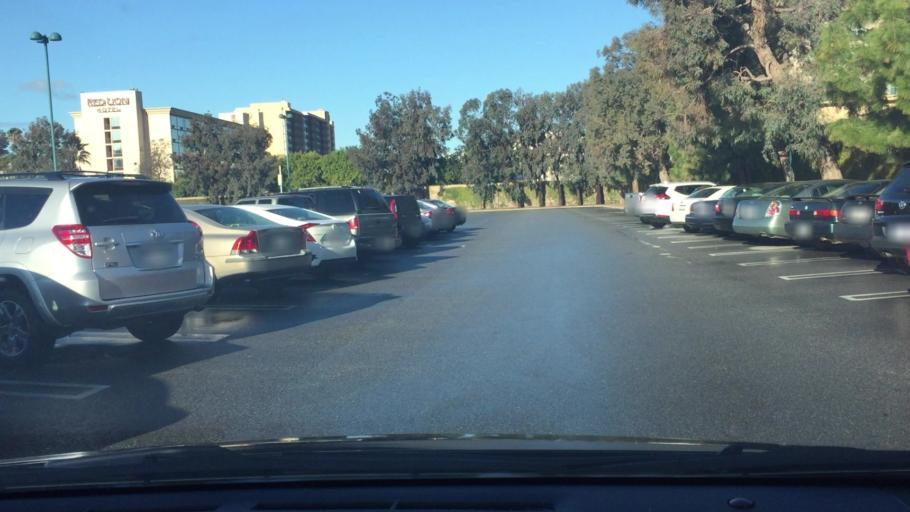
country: US
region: California
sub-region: Orange County
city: Anaheim
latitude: 33.8025
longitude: -117.9123
